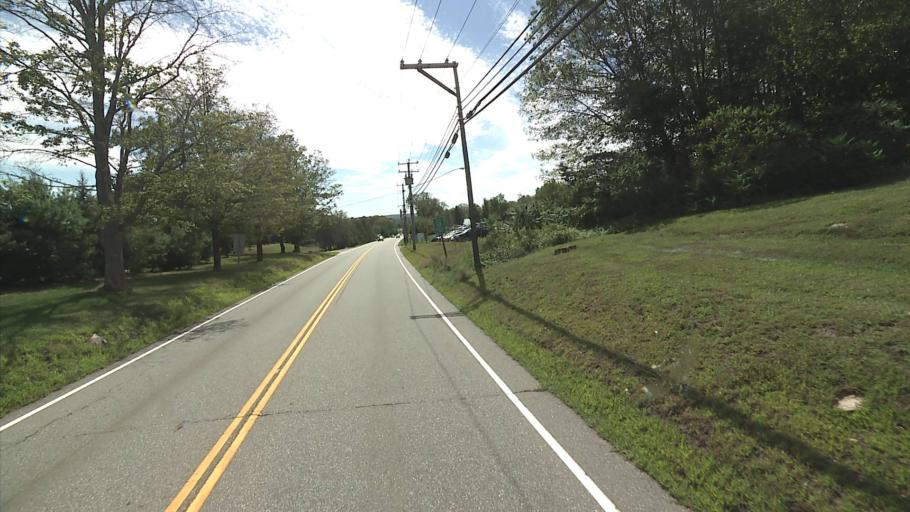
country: US
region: Connecticut
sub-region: Windham County
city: Willimantic
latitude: 41.7422
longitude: -72.1969
